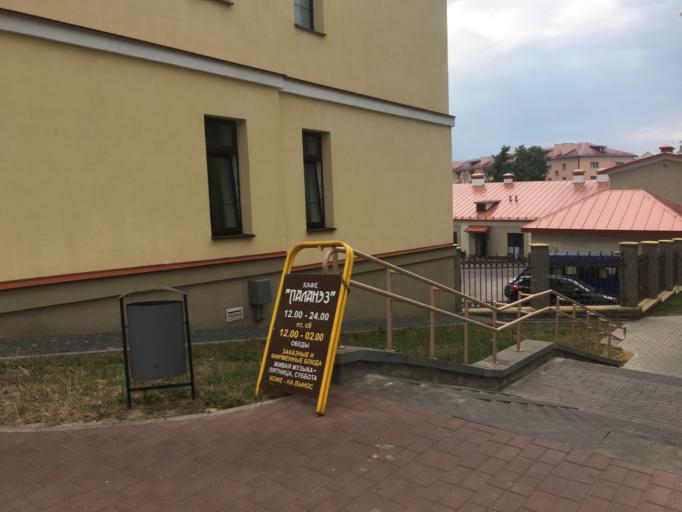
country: BY
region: Grodnenskaya
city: Hrodna
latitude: 53.6854
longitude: 23.8470
